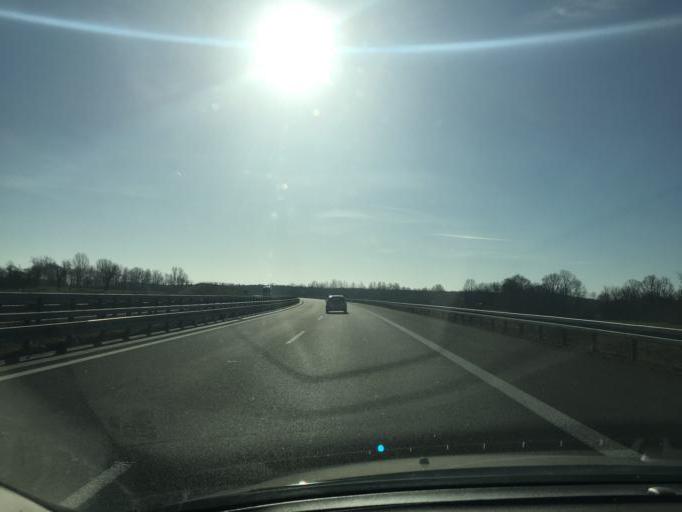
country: DE
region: Saxony
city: Frohburg
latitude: 51.0789
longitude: 12.5459
